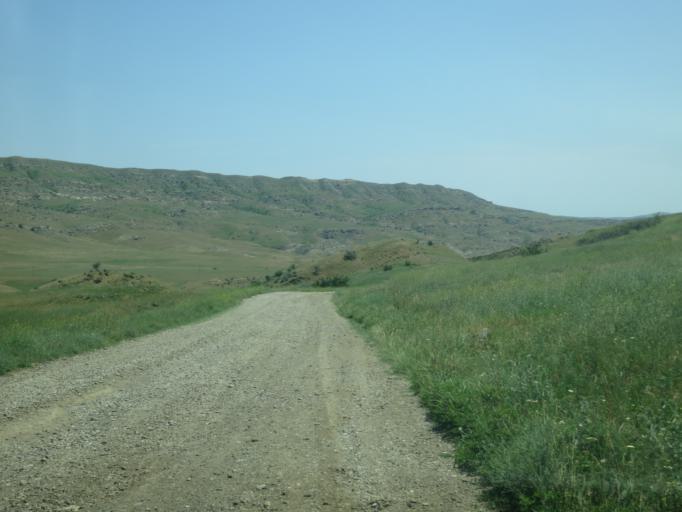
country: AZ
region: Agstafa
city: Saloglu
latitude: 41.4599
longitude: 45.3520
